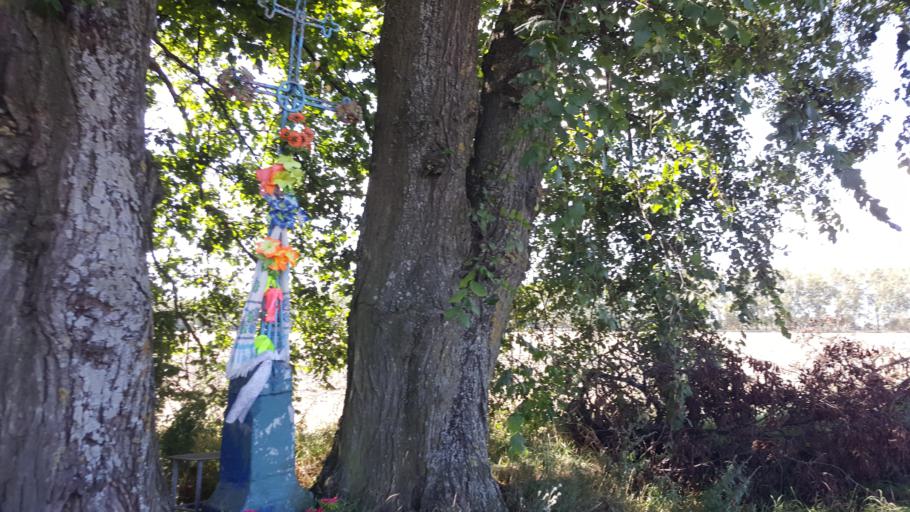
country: BY
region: Brest
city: Vysokaye
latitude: 52.2769
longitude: 23.3569
